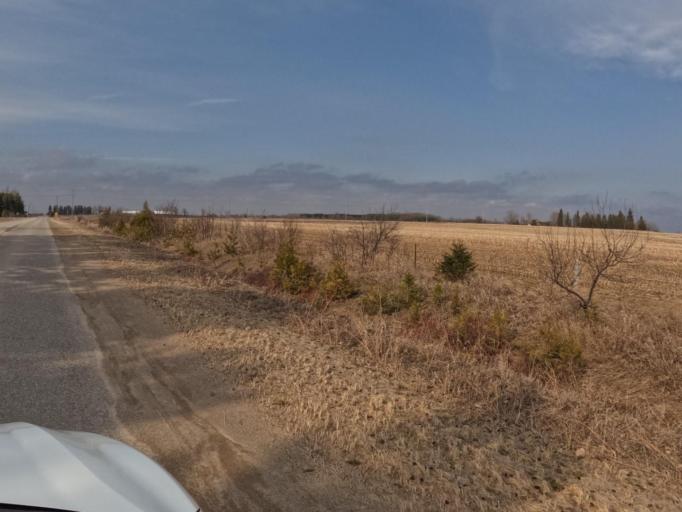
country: CA
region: Ontario
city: Orangeville
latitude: 43.9062
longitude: -80.2862
